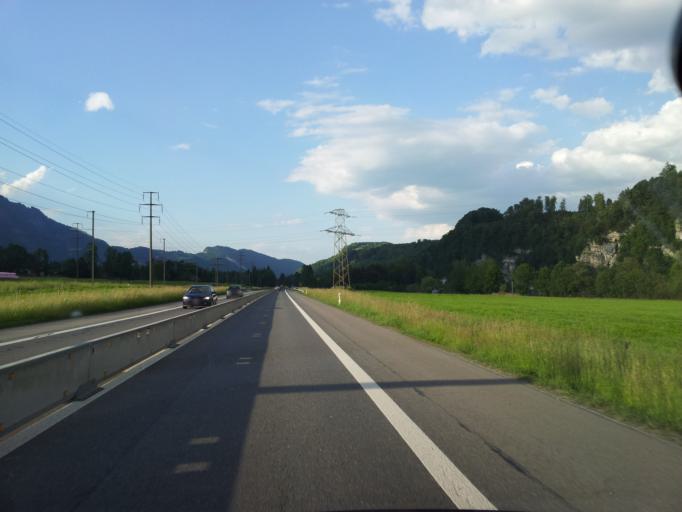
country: CH
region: Obwalden
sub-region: Obwalden
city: Kerns
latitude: 46.9185
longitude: 8.2691
